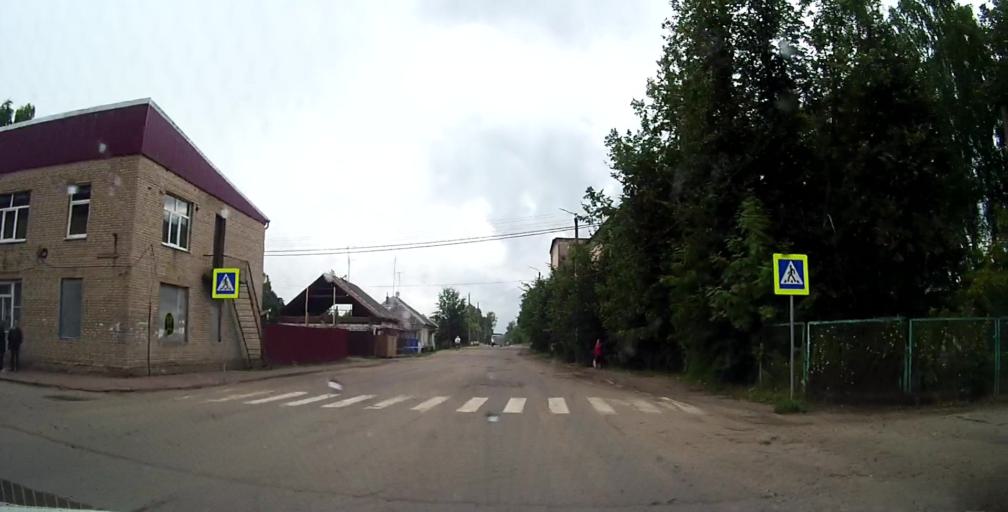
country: RU
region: Smolensk
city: Demidov
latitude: 55.2647
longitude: 31.5178
